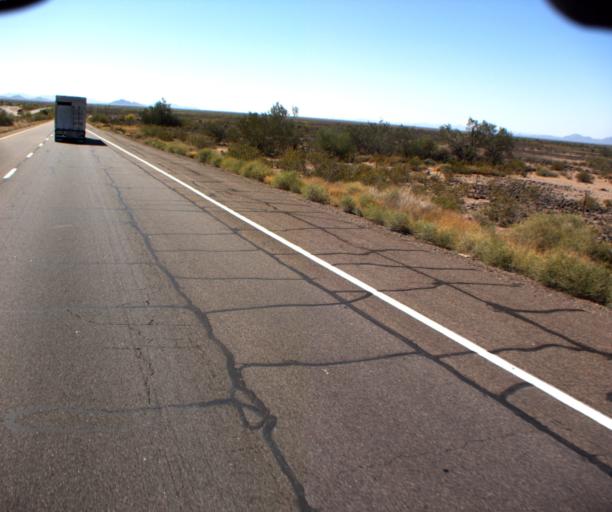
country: US
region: Arizona
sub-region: Maricopa County
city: Gila Bend
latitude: 32.8527
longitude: -113.2577
